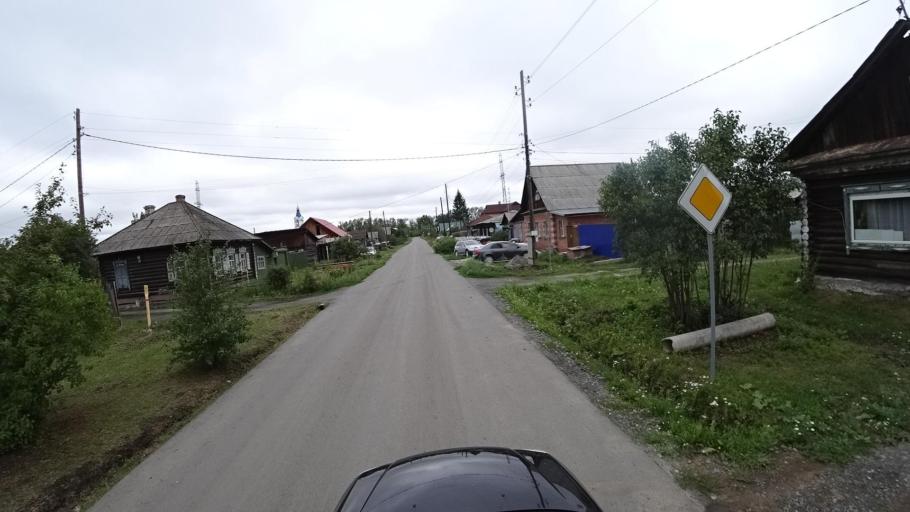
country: RU
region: Sverdlovsk
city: Kamyshlov
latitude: 56.8431
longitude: 62.7537
